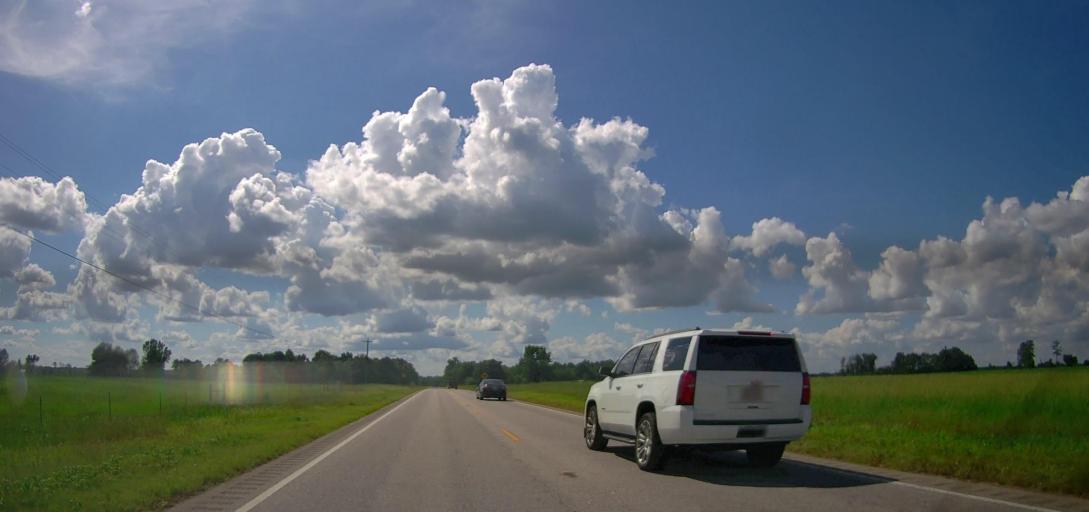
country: US
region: Alabama
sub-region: Lee County
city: Auburn
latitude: 32.4271
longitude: -85.4573
